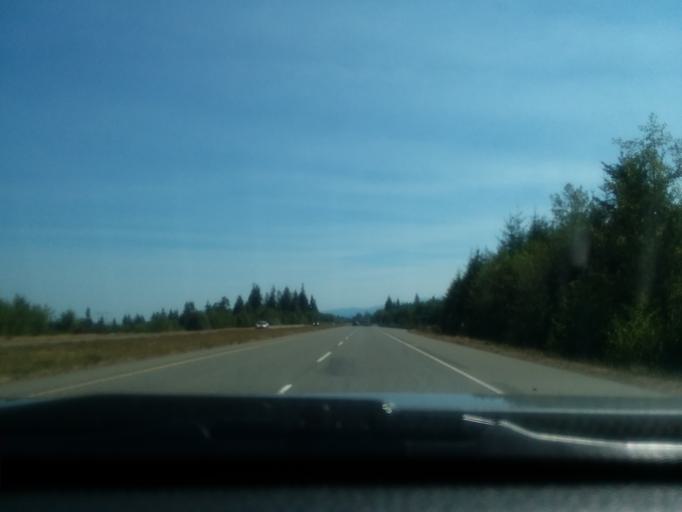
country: CA
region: British Columbia
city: Cumberland
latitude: 49.5266
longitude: -124.8627
